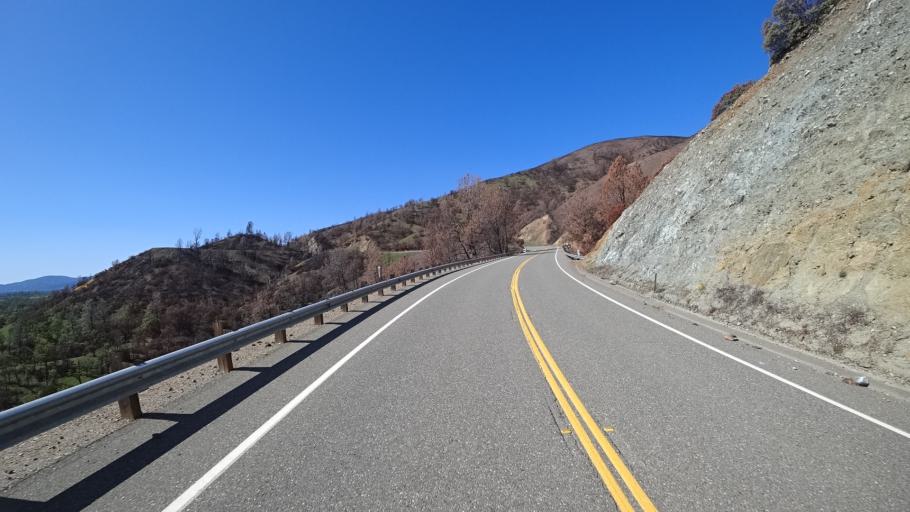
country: US
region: California
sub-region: Glenn County
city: Orland
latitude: 39.6493
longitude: -122.5947
